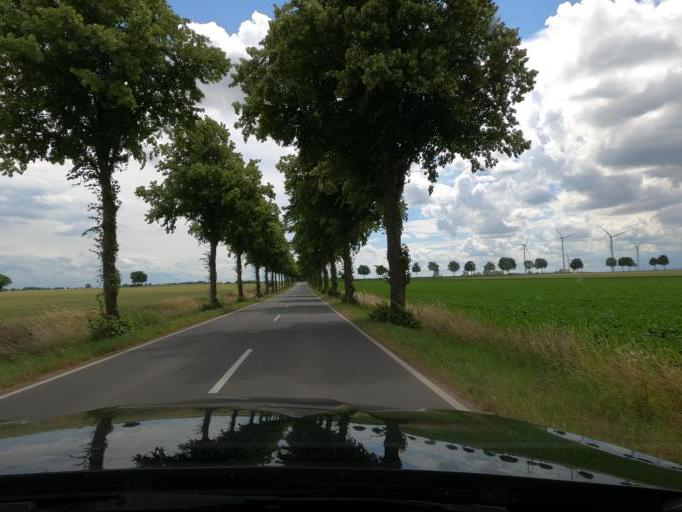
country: DE
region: Lower Saxony
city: Algermissen
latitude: 52.2664
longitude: 10.0116
